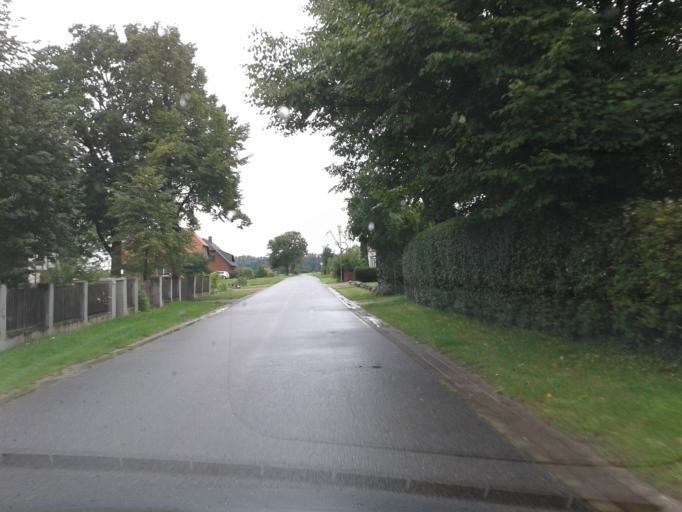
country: DE
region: Lower Saxony
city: Woltersdorf
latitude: 52.9432
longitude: 11.1861
